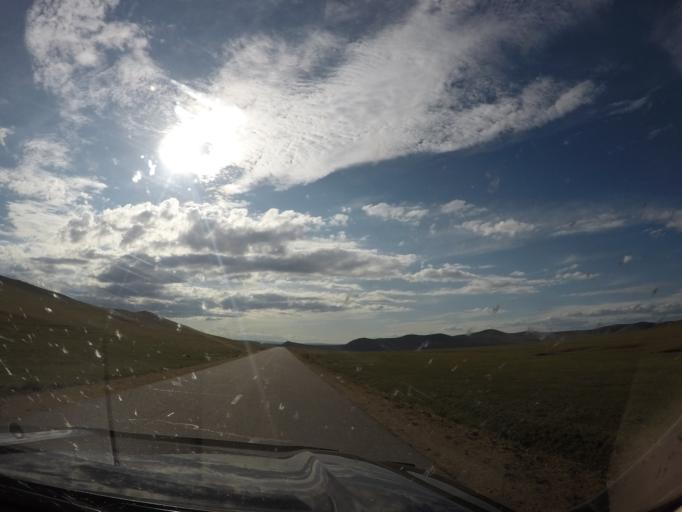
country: MN
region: Central Aimak
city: Bayandelger
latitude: 47.6937
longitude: 108.5065
